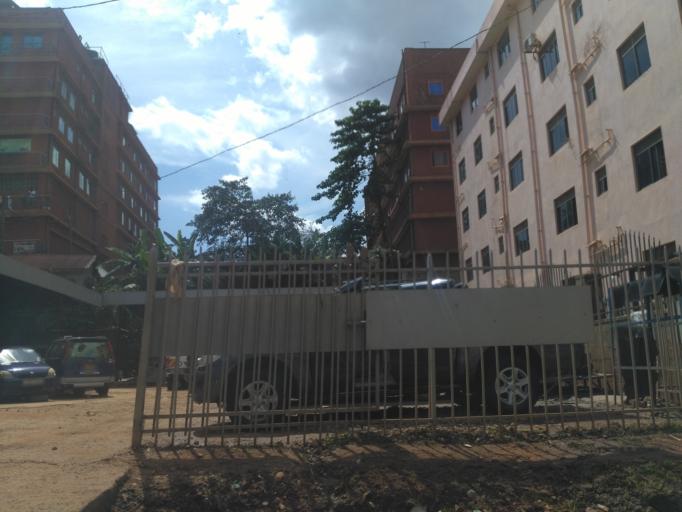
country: UG
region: Central Region
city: Kampala Central Division
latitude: 0.3344
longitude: 32.5738
